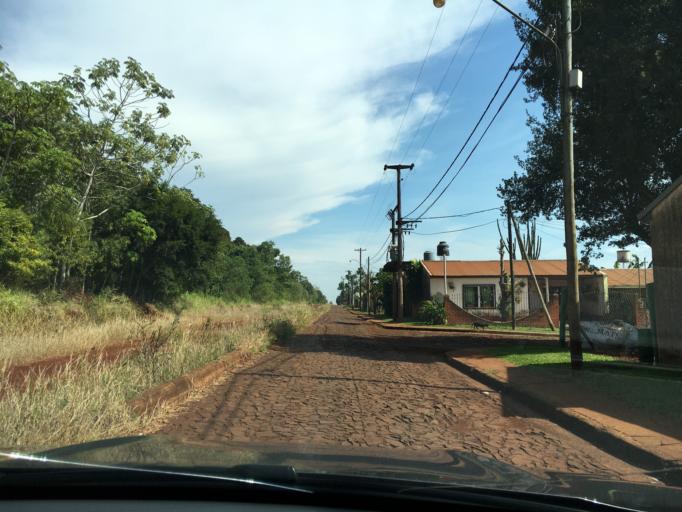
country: AR
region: Misiones
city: Puerto Rico
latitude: -26.8047
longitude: -55.0005
